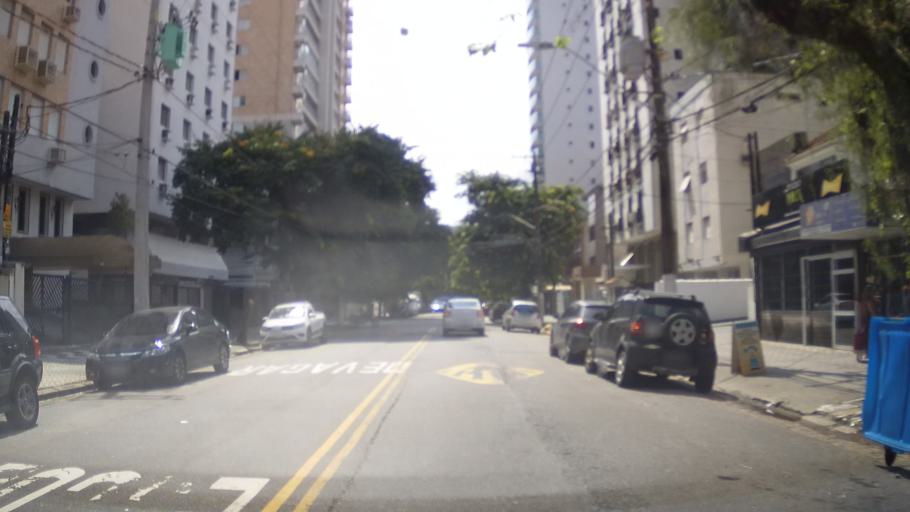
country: BR
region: Sao Paulo
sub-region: Santos
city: Santos
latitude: -23.9635
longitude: -46.3365
